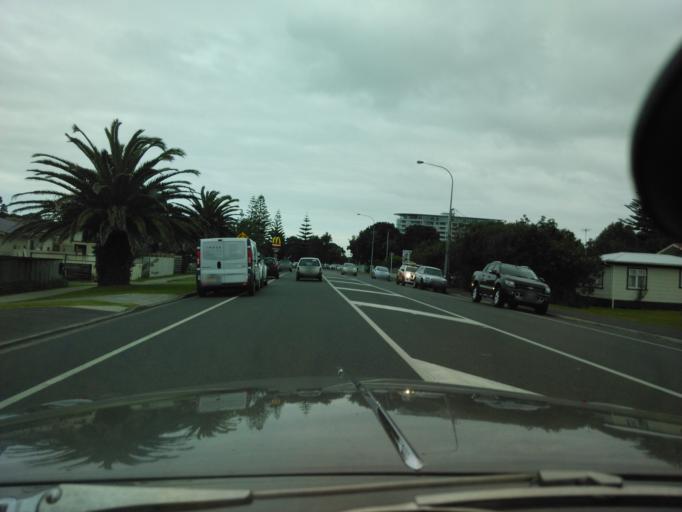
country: NZ
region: Auckland
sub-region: Auckland
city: Rothesay Bay
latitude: -36.5828
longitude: 174.6939
